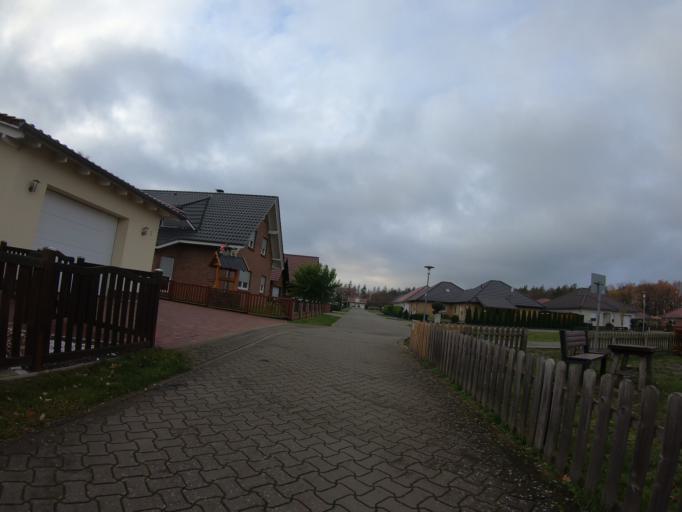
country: DE
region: Lower Saxony
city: Wesendorf
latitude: 52.5823
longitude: 10.5327
